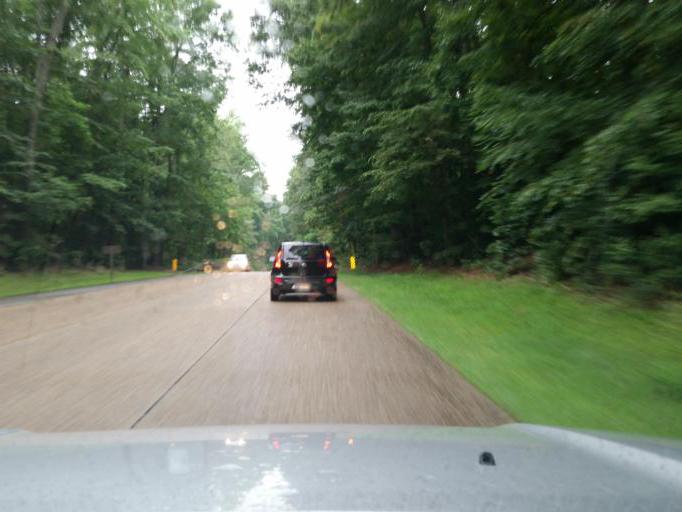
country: US
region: Virginia
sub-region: City of Williamsburg
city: Williamsburg
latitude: 37.2790
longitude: -76.6713
